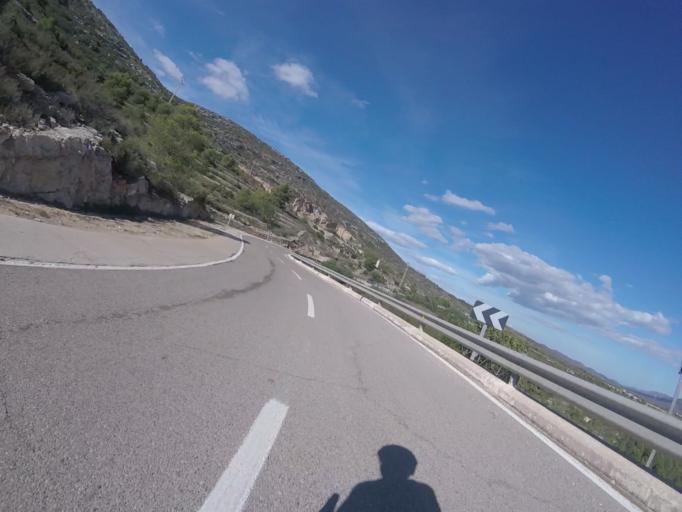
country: ES
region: Valencia
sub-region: Provincia de Castello
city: Alcala de Xivert
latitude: 40.2966
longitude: 0.1866
